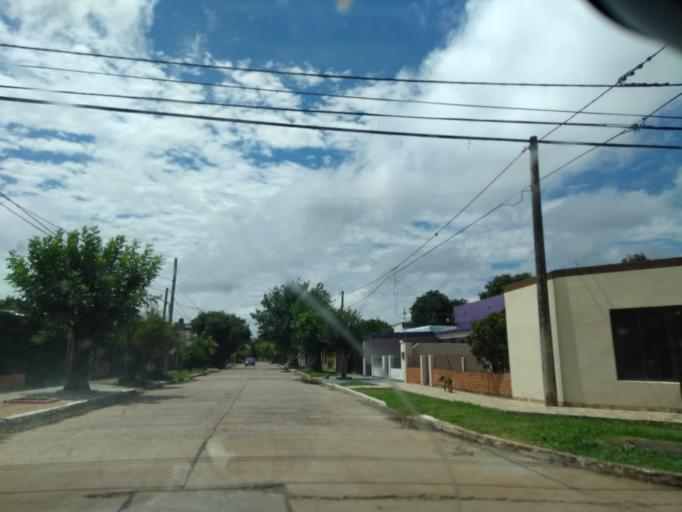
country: AR
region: Chaco
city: Barranqueras
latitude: -27.4800
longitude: -58.9528
